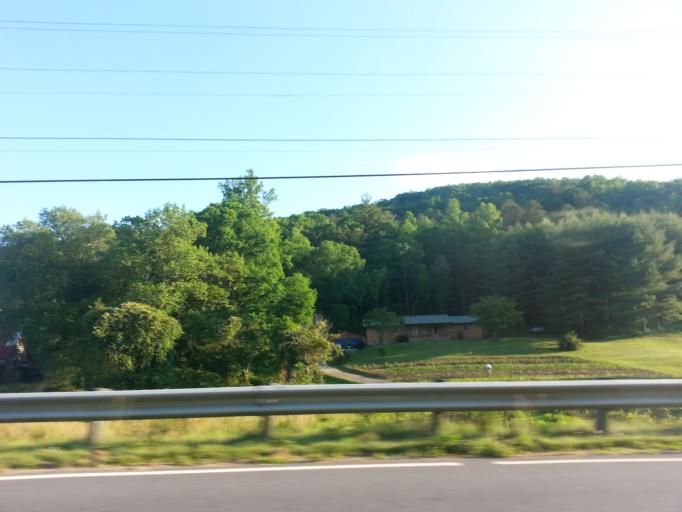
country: US
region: North Carolina
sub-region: Cherokee County
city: Murphy
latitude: 35.0519
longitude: -84.1546
